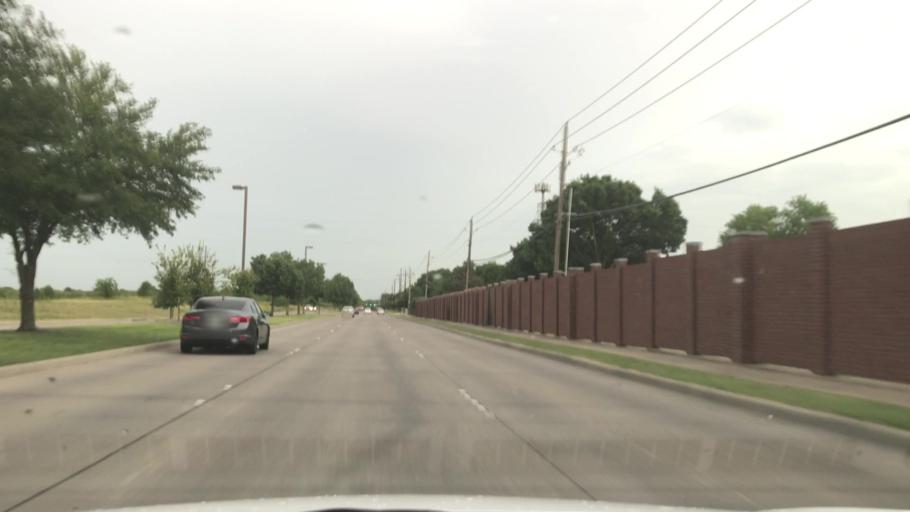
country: US
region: Texas
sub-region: Dallas County
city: Mesquite
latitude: 32.7437
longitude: -96.5790
